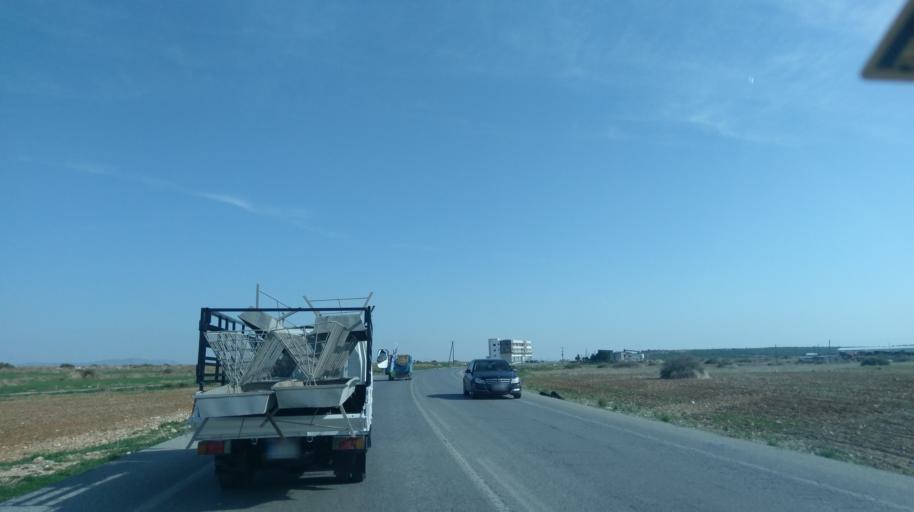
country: CY
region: Larnaka
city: Athienou
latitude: 35.2323
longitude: 33.5614
